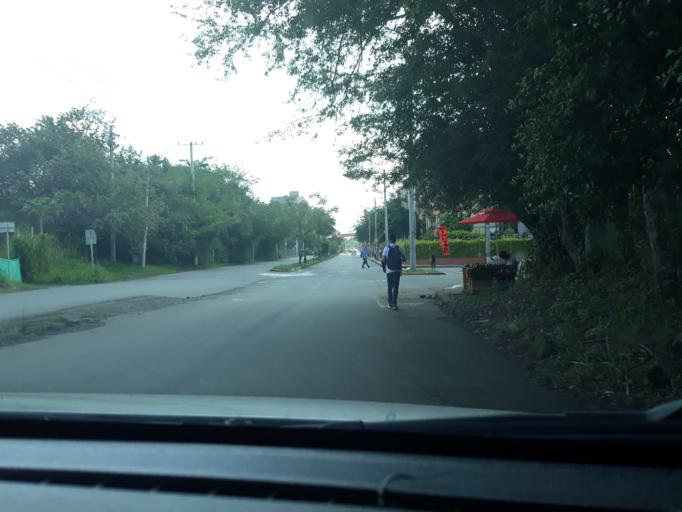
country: CO
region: Valle del Cauca
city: Cali
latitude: 3.3588
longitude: -76.5208
